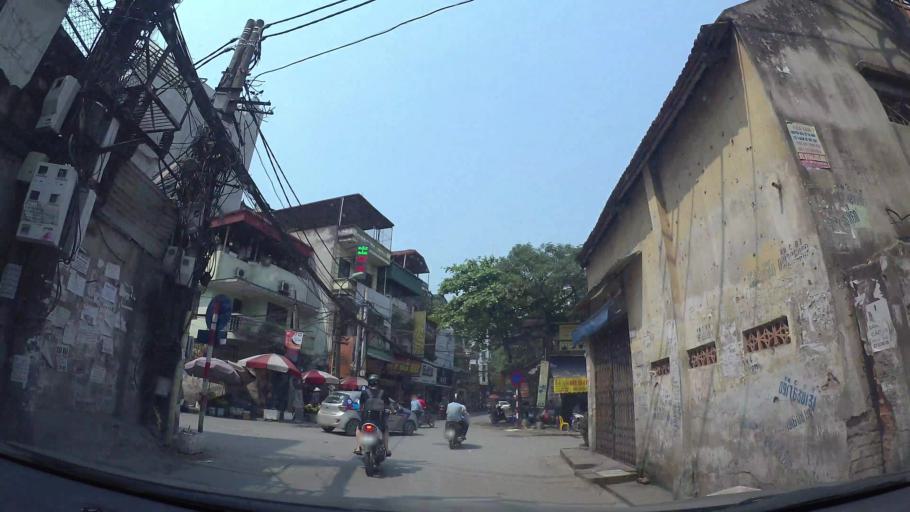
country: VN
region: Ha Noi
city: Thanh Xuan
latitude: 21.0070
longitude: 105.8120
